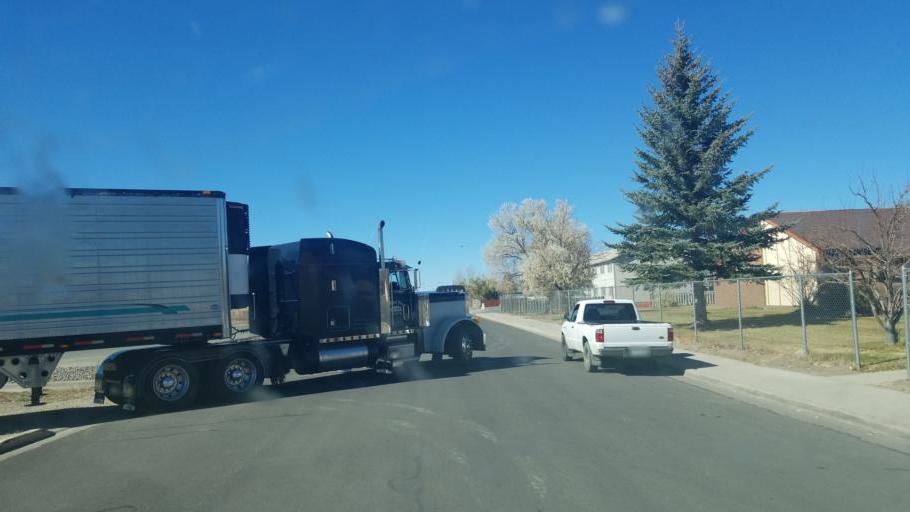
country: US
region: Colorado
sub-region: Alamosa County
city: Alamosa
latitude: 37.4763
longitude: -105.8906
